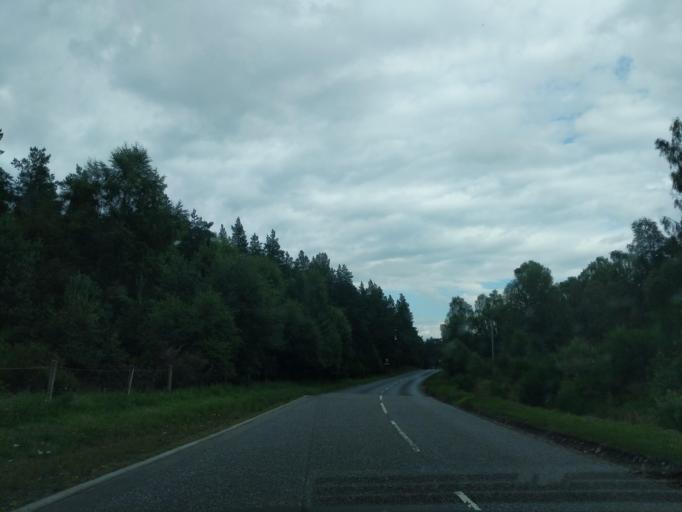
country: GB
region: Scotland
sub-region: Highland
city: Aviemore
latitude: 57.2990
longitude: -3.7787
